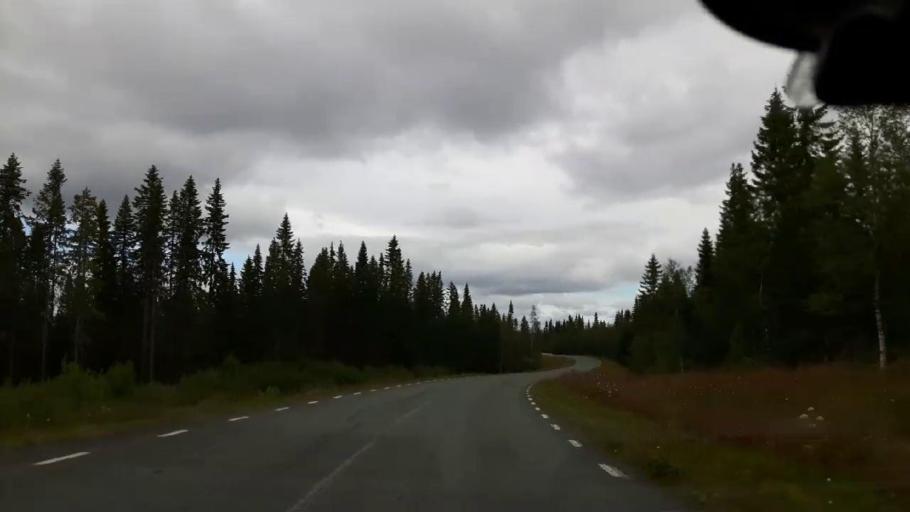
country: SE
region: Jaemtland
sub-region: Krokoms Kommun
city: Valla
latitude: 63.5446
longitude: 13.8542
